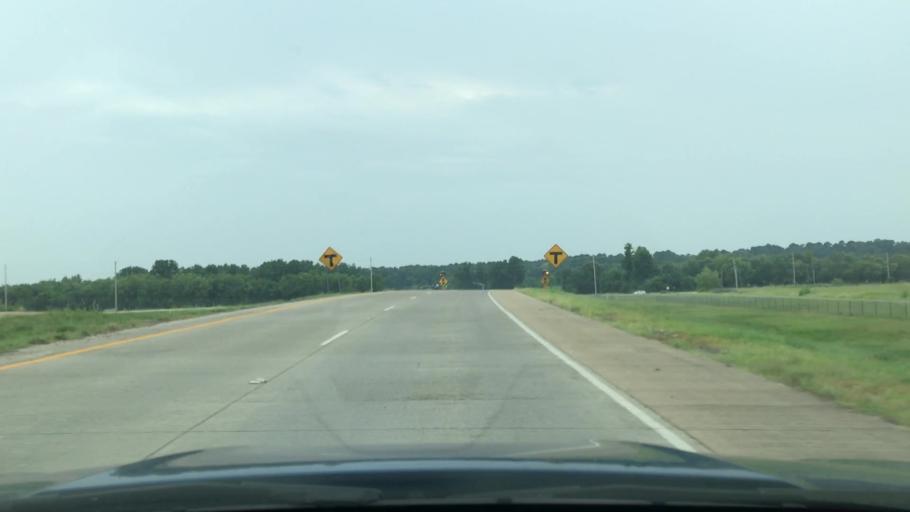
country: US
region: Louisiana
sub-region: Bossier Parish
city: Bossier City
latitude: 32.4034
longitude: -93.7149
